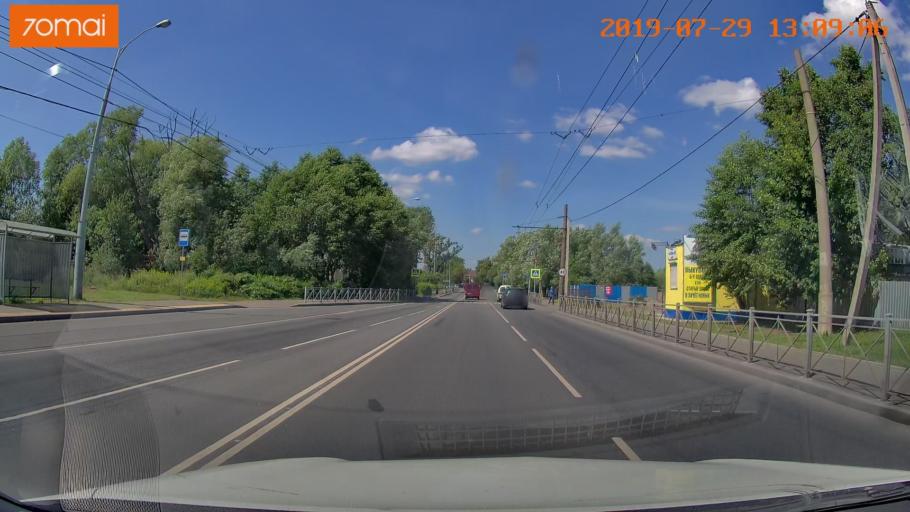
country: RU
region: Kaliningrad
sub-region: Gorod Kaliningrad
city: Kaliningrad
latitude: 54.7130
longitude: 20.4219
